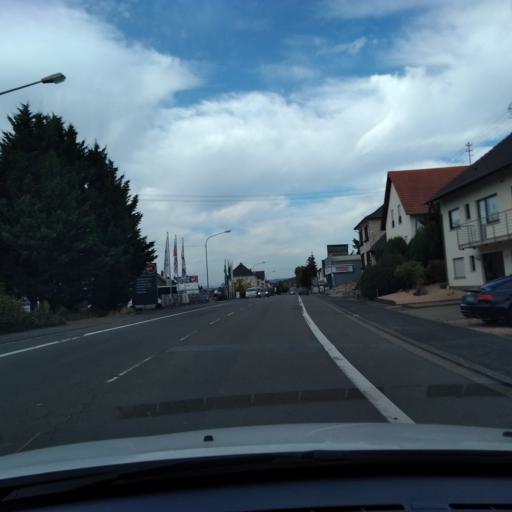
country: DE
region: Saarland
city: Ensdorf
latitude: 49.2965
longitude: 6.7779
